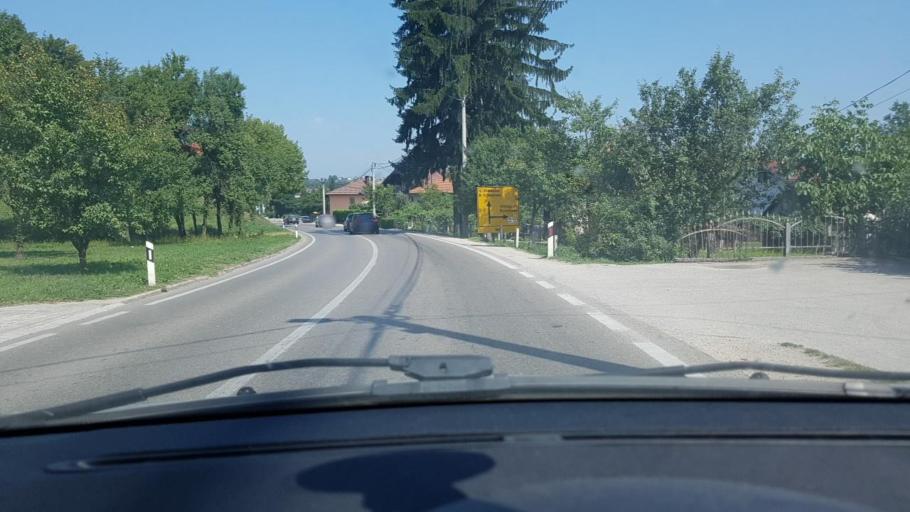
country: BA
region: Federation of Bosnia and Herzegovina
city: Velika Kladusa
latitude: 45.1785
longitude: 15.8209
